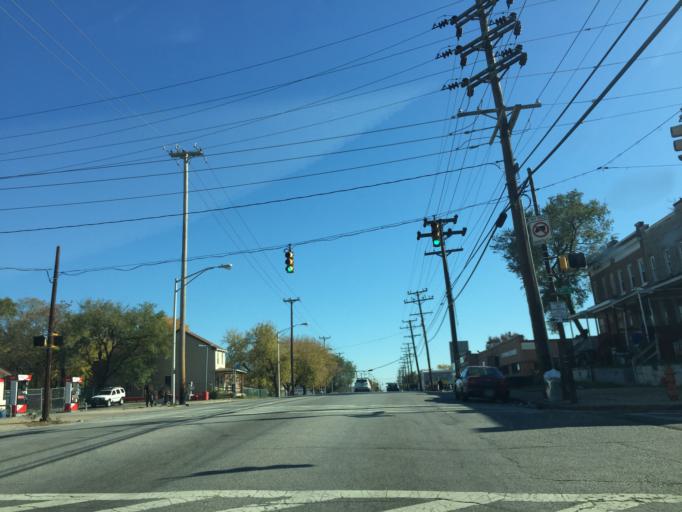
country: US
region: Maryland
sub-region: Anne Arundel County
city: Brooklyn Park
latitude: 39.2349
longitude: -76.5979
